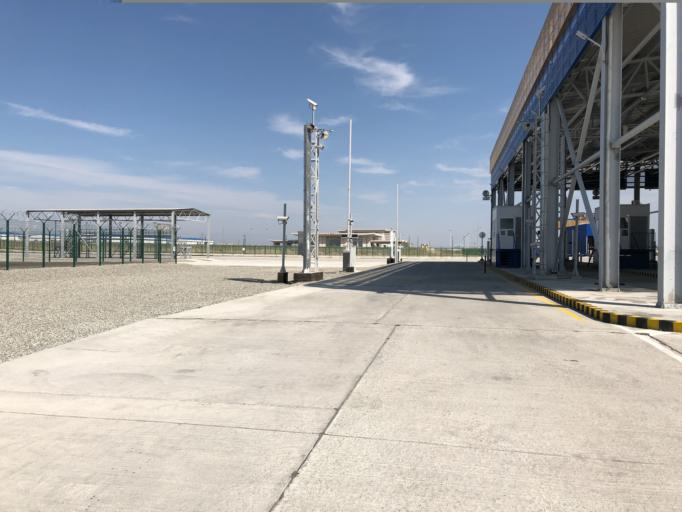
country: KZ
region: Almaty Oblysy
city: Zharkent
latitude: 44.1578
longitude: 80.3984
